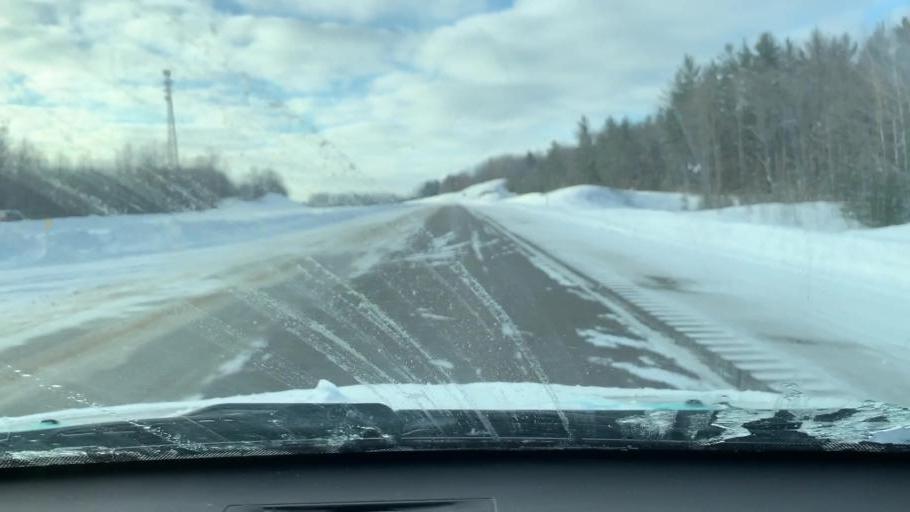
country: US
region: Michigan
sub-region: Wexford County
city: Manton
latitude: 44.3377
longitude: -85.4062
